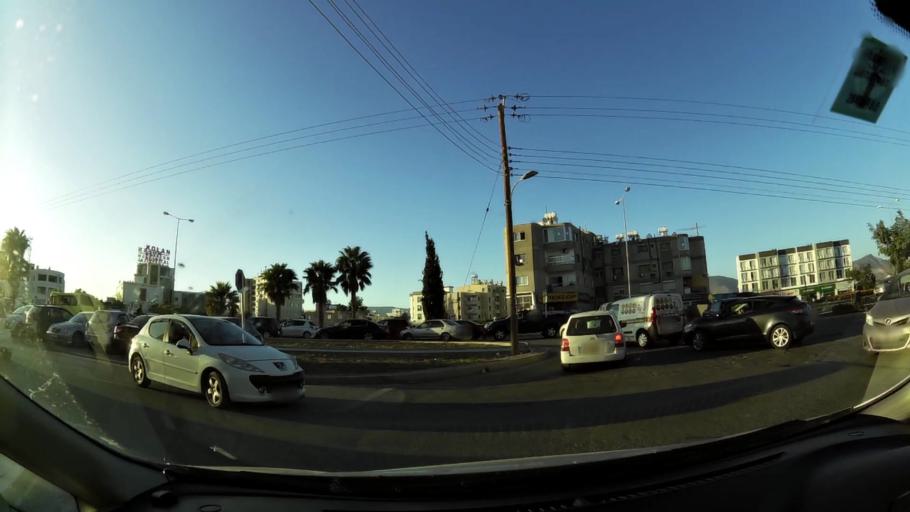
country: CY
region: Lefkosia
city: Nicosia
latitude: 35.2083
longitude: 33.3183
